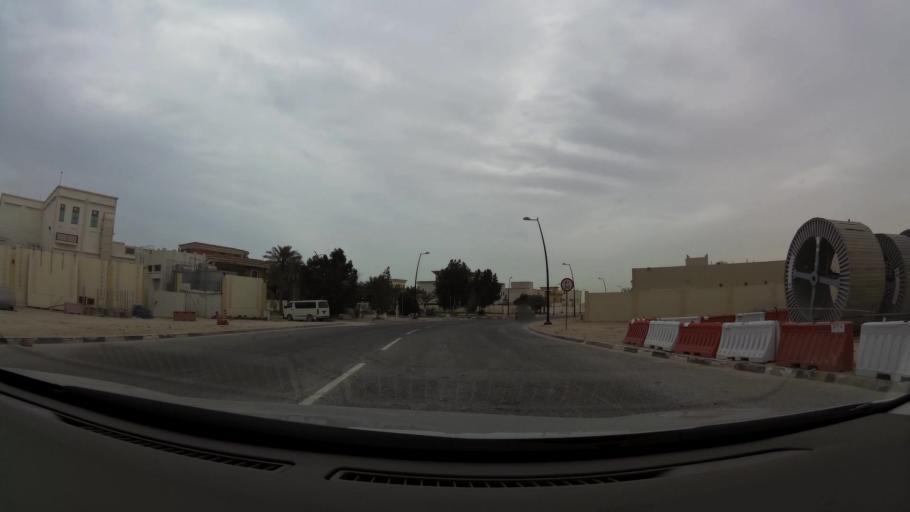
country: QA
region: Baladiyat ad Dawhah
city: Doha
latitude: 25.3488
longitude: 51.4997
